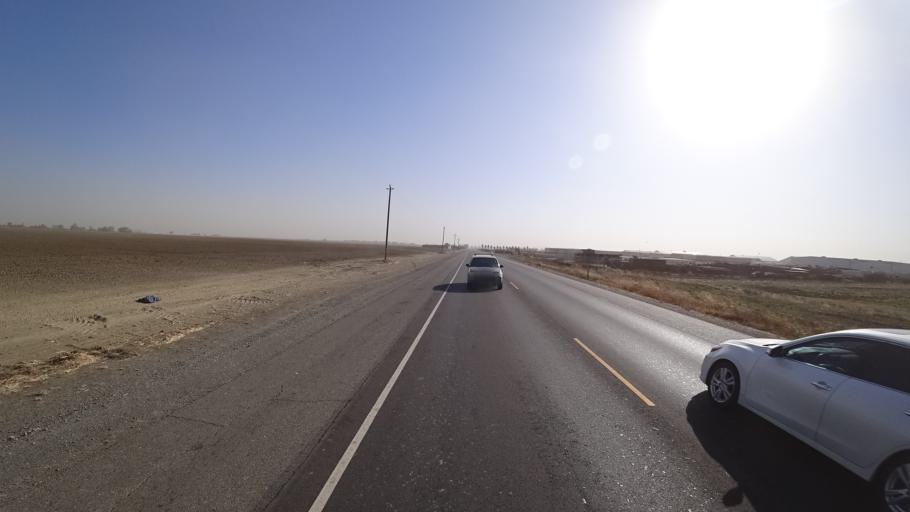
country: US
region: California
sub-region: Yolo County
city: Woodland
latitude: 38.7558
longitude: -121.7291
